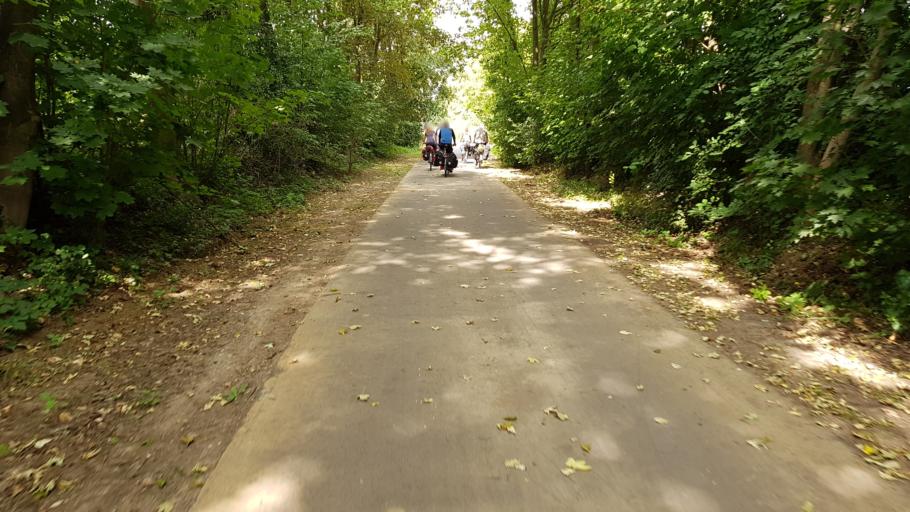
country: PL
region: West Pomeranian Voivodeship
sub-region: Powiat pyrzycki
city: Pyrzyce
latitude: 53.1335
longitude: 14.9779
